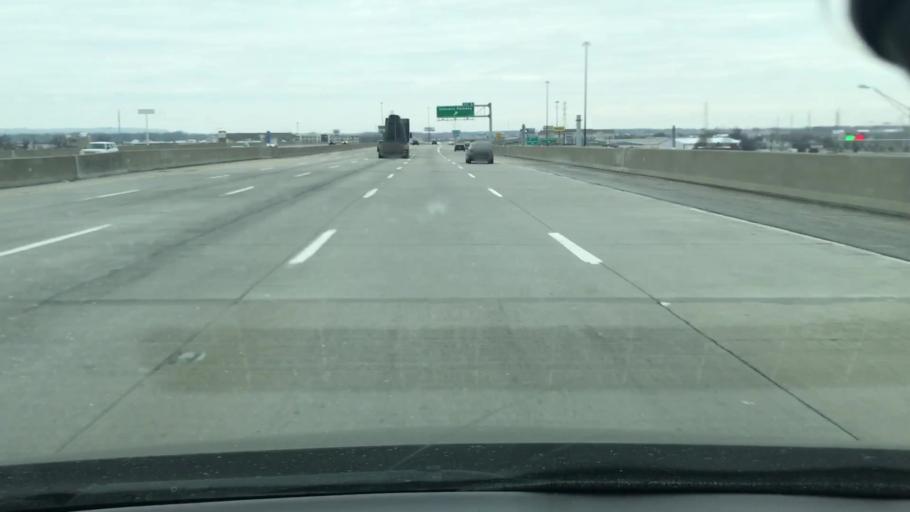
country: US
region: Indiana
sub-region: Clark County
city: Clarksville
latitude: 38.3186
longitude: -85.7528
